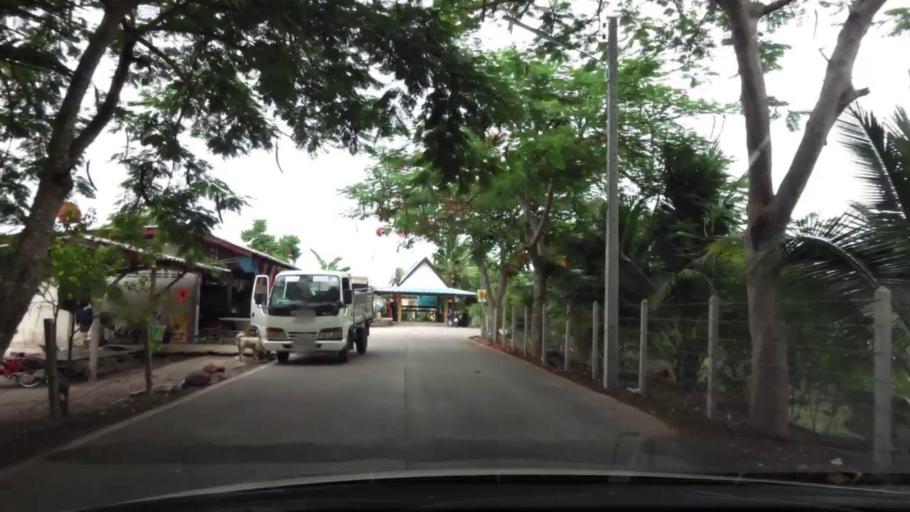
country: TH
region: Samut Sakhon
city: Ban Phaeo
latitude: 13.5649
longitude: 100.0365
